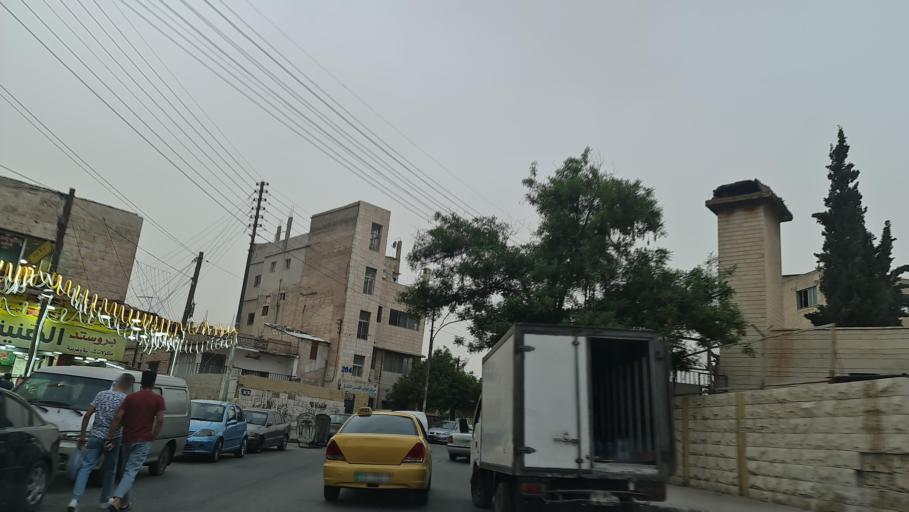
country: JO
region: Amman
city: Amman
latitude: 31.9414
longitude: 35.9385
